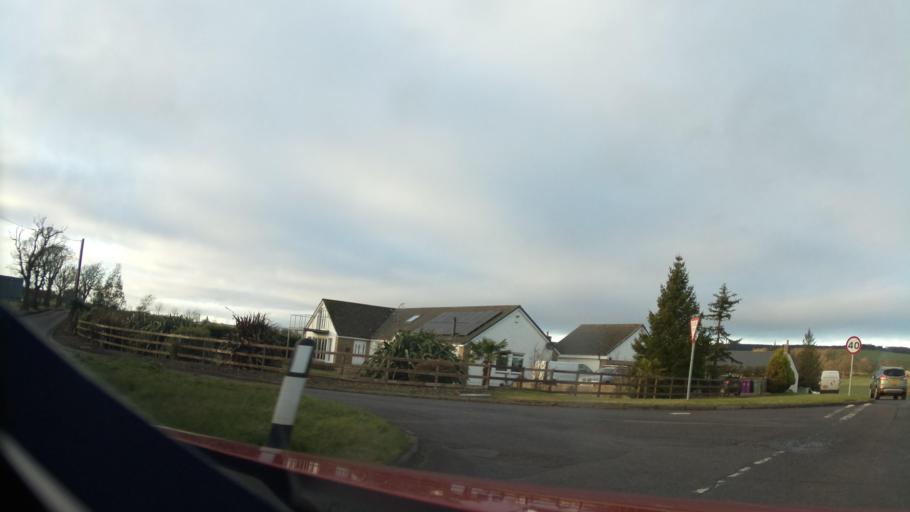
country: GB
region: Scotland
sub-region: Fife
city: Tayport
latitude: 56.5093
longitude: -2.8177
